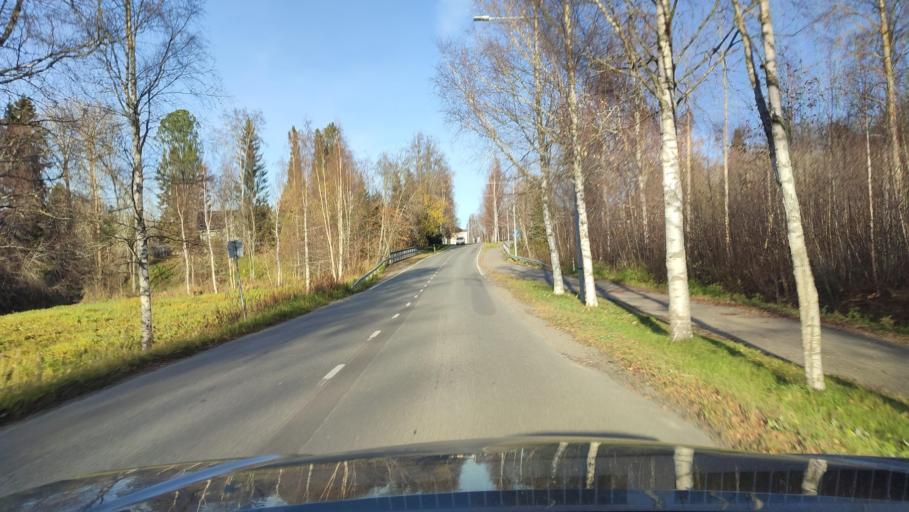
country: FI
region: Southern Ostrobothnia
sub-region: Suupohja
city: Teuva
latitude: 62.4768
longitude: 21.7411
